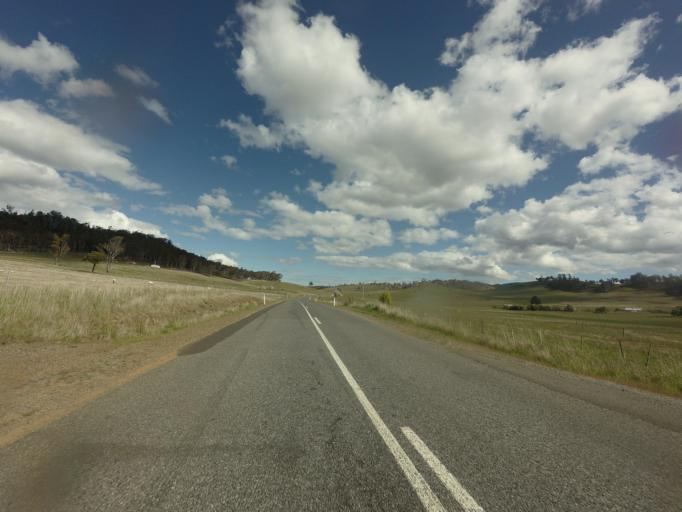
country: AU
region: Tasmania
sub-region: Brighton
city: Bridgewater
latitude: -42.4791
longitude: 147.3262
